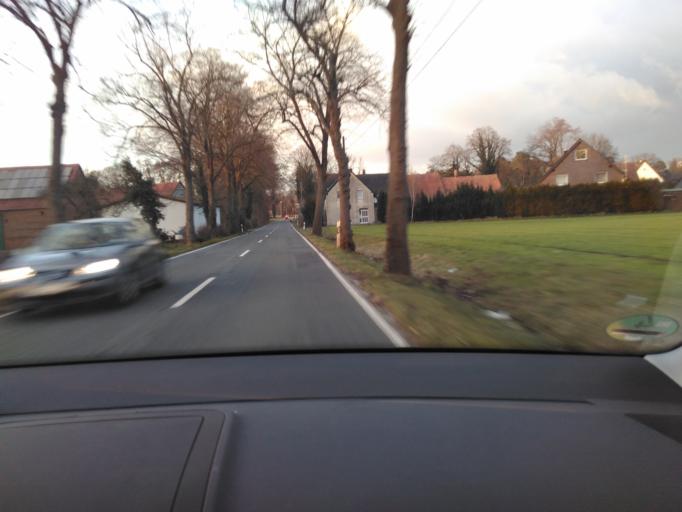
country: DE
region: North Rhine-Westphalia
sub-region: Regierungsbezirk Detmold
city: Verl
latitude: 51.9443
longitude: 8.4910
